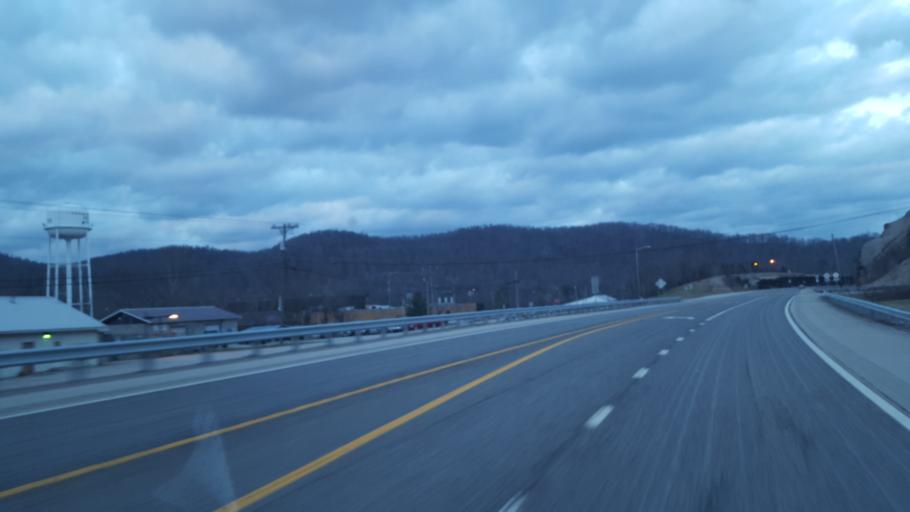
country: US
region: Kentucky
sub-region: Lewis County
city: Vanceburg
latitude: 38.5947
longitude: -83.3455
